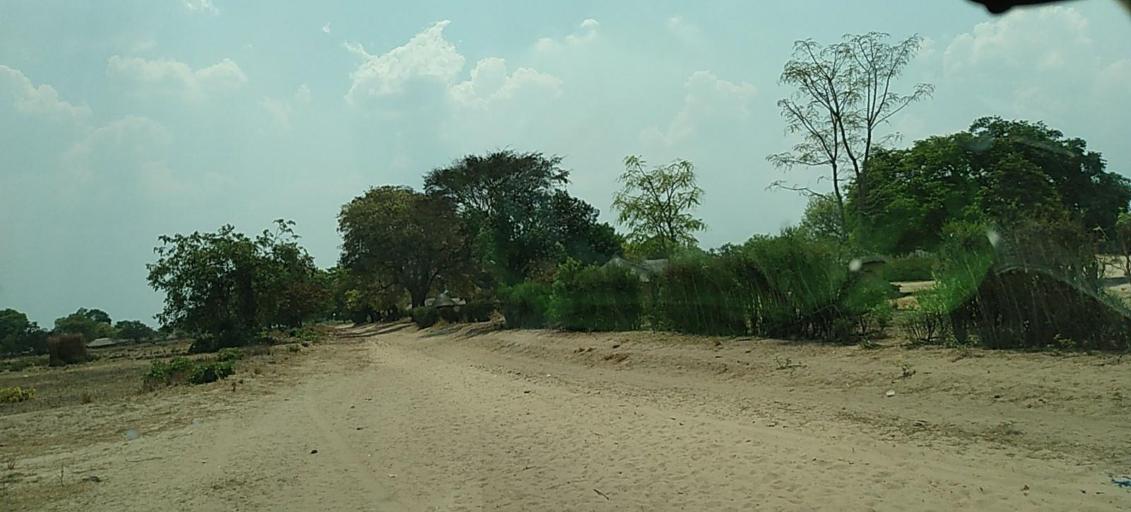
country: ZM
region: North-Western
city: Kabompo
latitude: -13.4018
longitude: 23.8214
